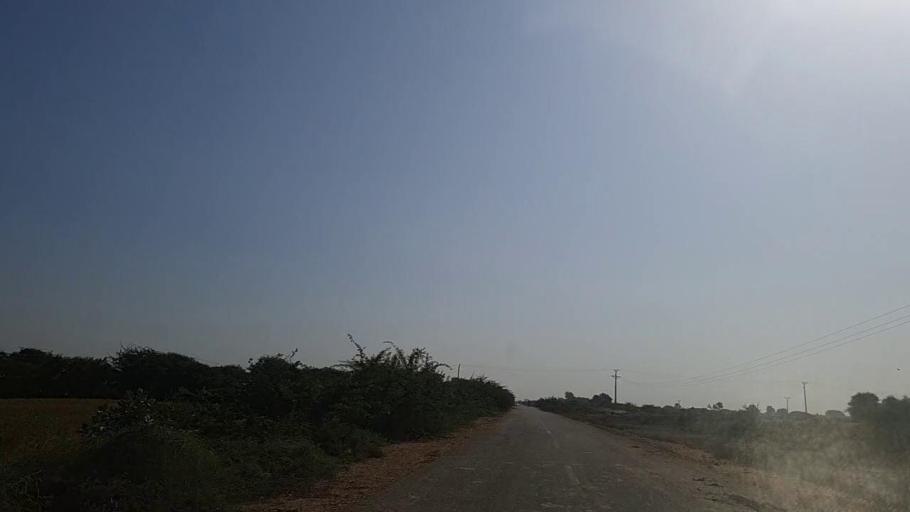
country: PK
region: Sindh
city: Jati
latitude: 24.4561
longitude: 68.2648
